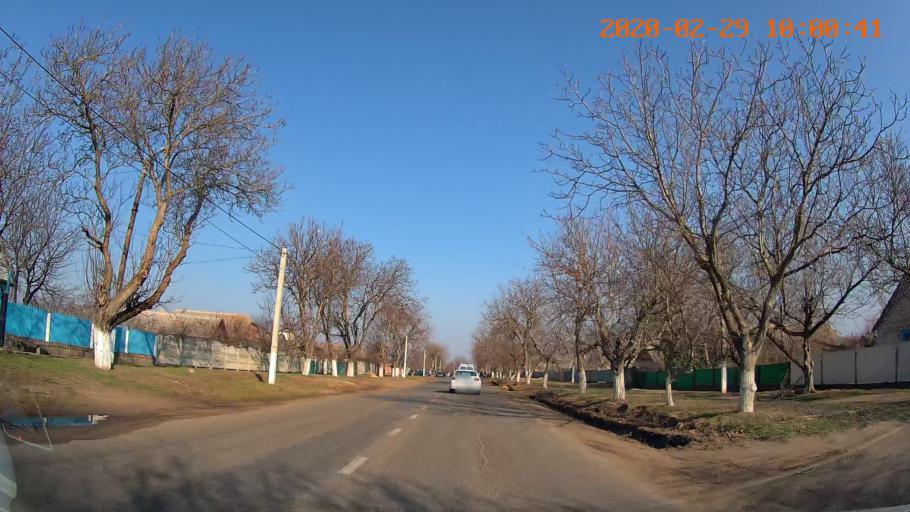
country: MD
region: Telenesti
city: Slobozia
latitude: 46.7702
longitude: 29.6860
